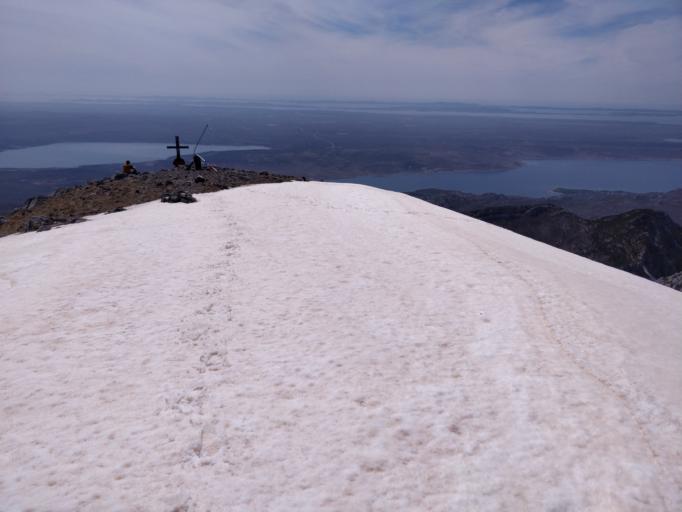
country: HR
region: Zadarska
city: Starigrad
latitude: 44.3287
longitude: 15.5697
